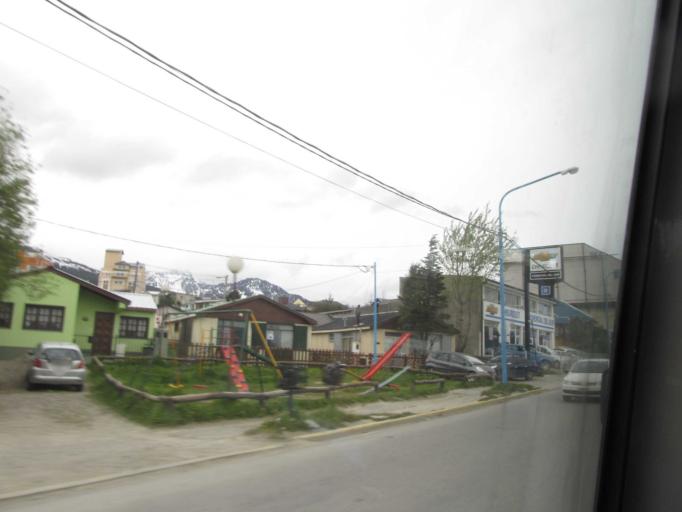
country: AR
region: Tierra del Fuego
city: Ushuaia
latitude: -54.8092
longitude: -68.3230
